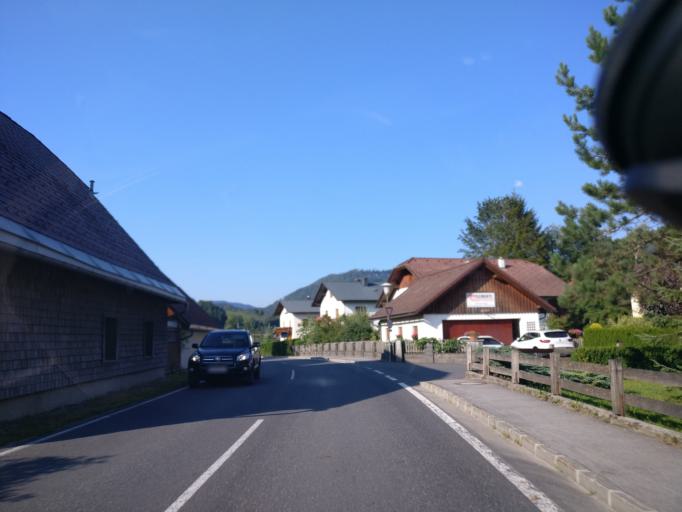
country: AT
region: Lower Austria
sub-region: Politischer Bezirk Scheibbs
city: Gostling an der Ybbs
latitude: 47.7927
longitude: 14.9187
